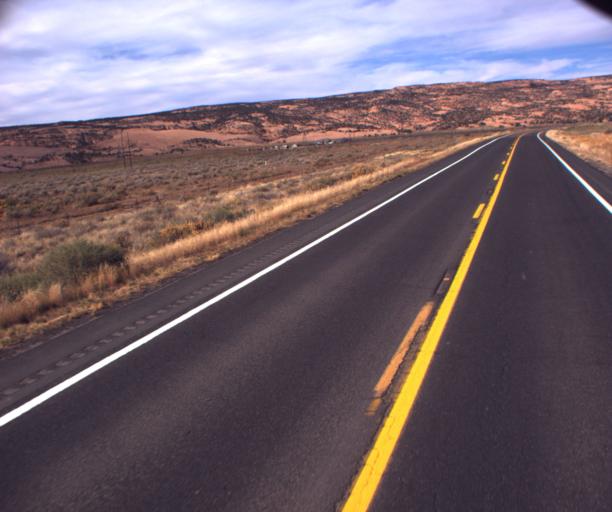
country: US
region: Arizona
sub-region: Navajo County
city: Kayenta
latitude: 36.6061
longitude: -110.4729
